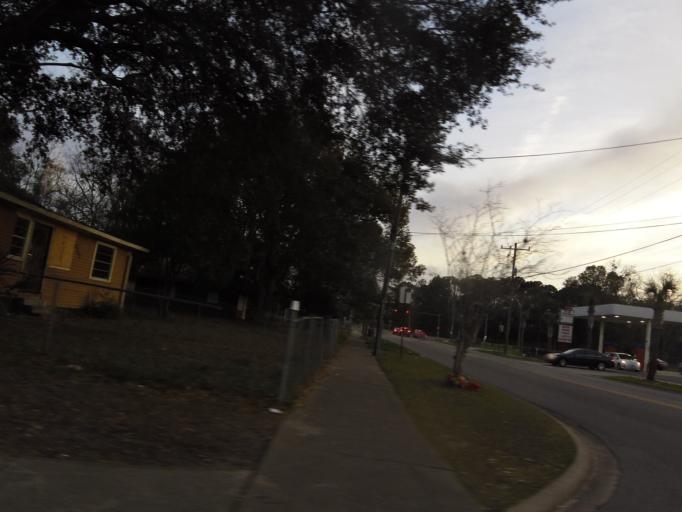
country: US
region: Florida
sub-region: Duval County
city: Jacksonville
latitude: 30.3579
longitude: -81.7014
